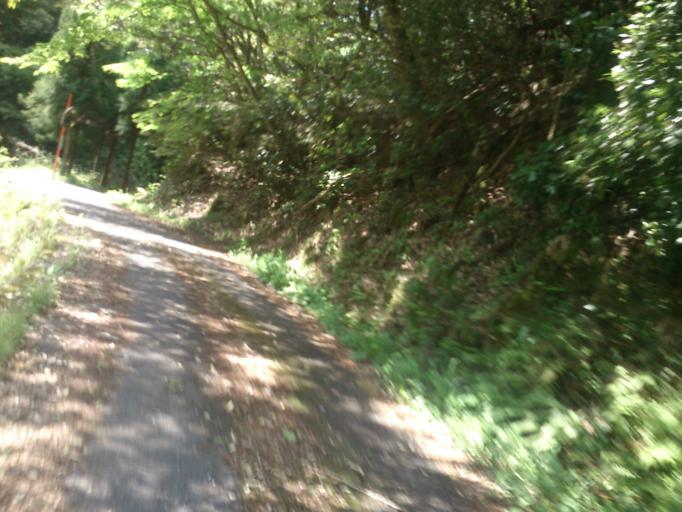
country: JP
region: Kyoto
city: Miyazu
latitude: 35.7034
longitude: 135.1189
